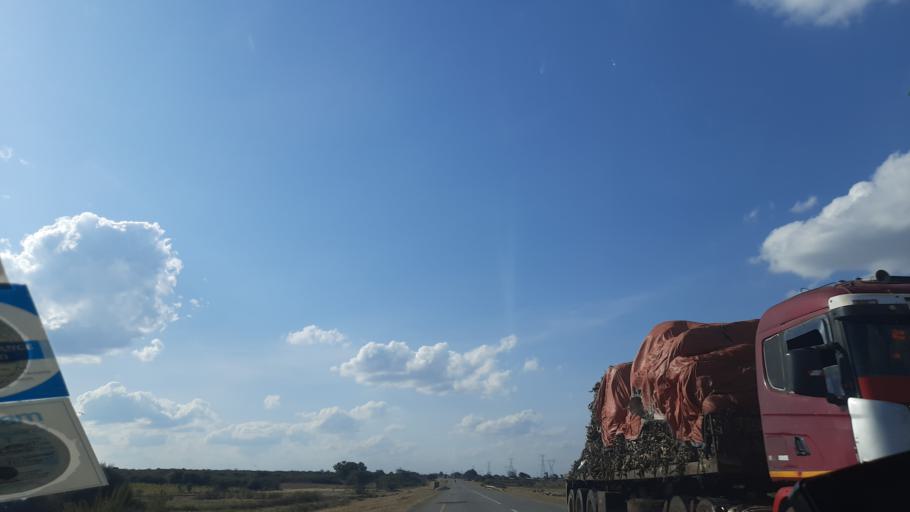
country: TZ
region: Singida
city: Ikungi
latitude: -5.1839
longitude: 34.7826
